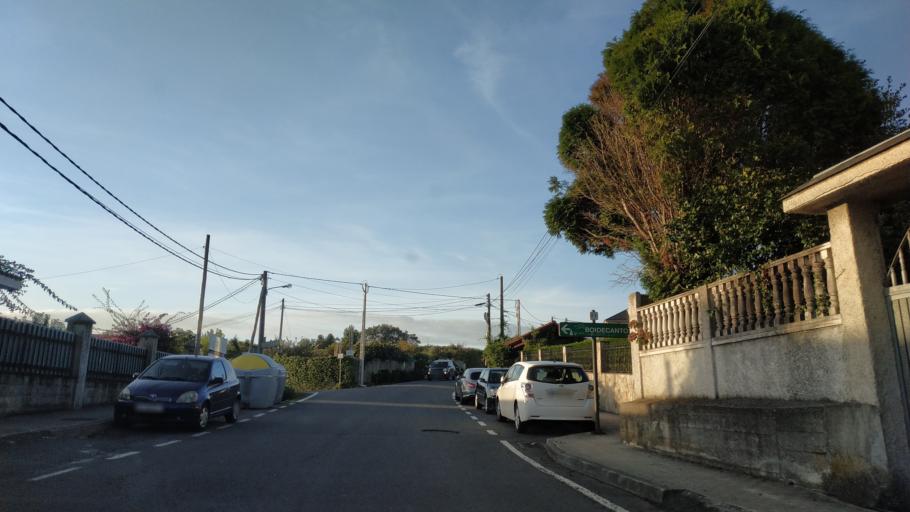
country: ES
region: Galicia
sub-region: Provincia da Coruna
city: Oleiros
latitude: 43.3559
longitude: -8.3437
